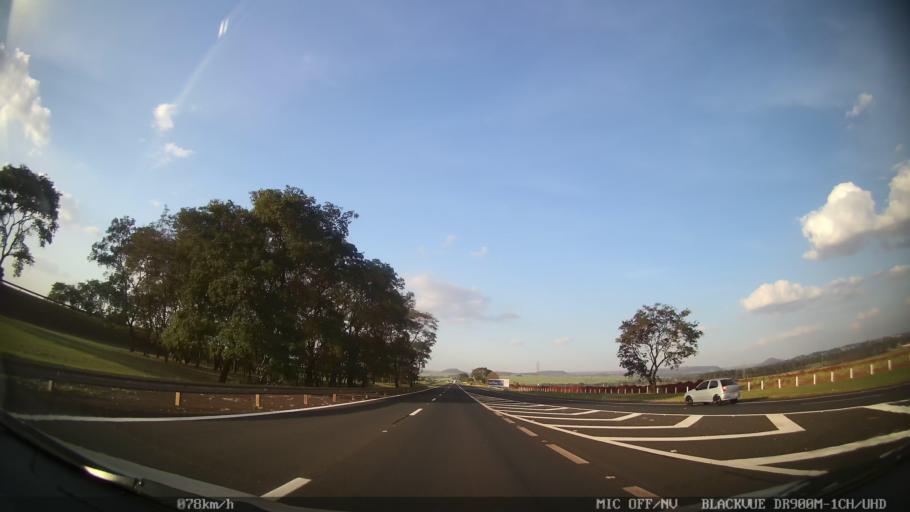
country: BR
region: Sao Paulo
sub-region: Ribeirao Preto
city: Ribeirao Preto
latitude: -21.1125
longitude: -47.7778
